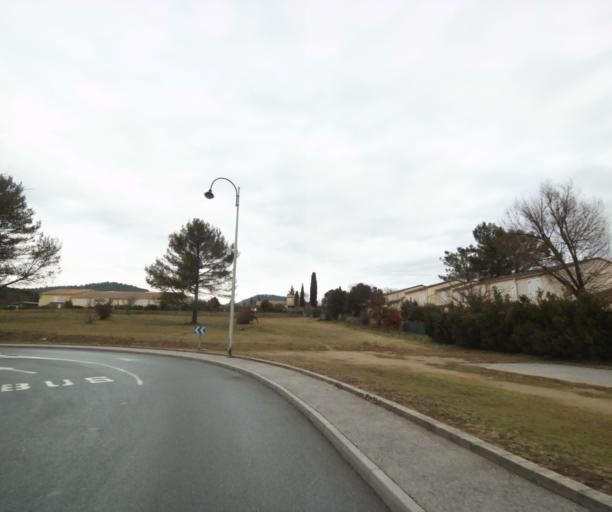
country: FR
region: Provence-Alpes-Cote d'Azur
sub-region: Departement du Var
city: Brignoles
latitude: 43.4130
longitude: 6.0665
